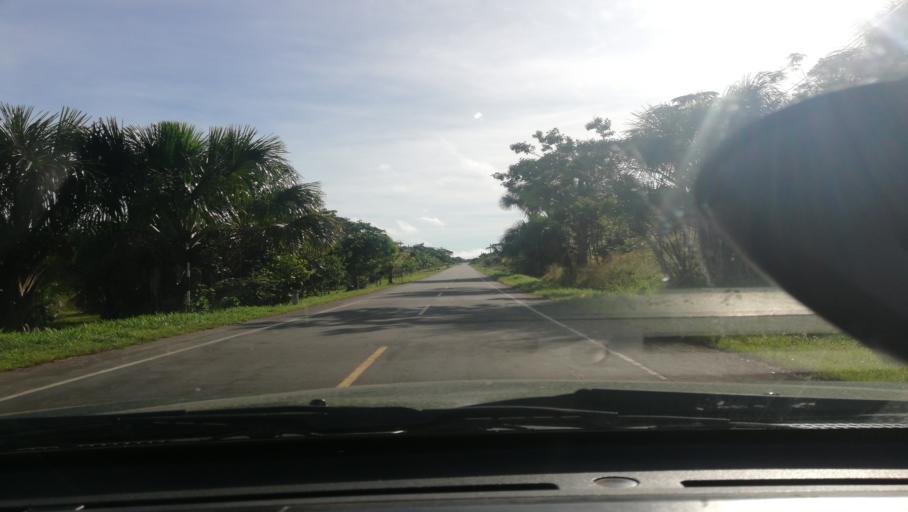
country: PE
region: Loreto
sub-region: Provincia de Loreto
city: Nauta
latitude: -4.3638
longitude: -73.5581
